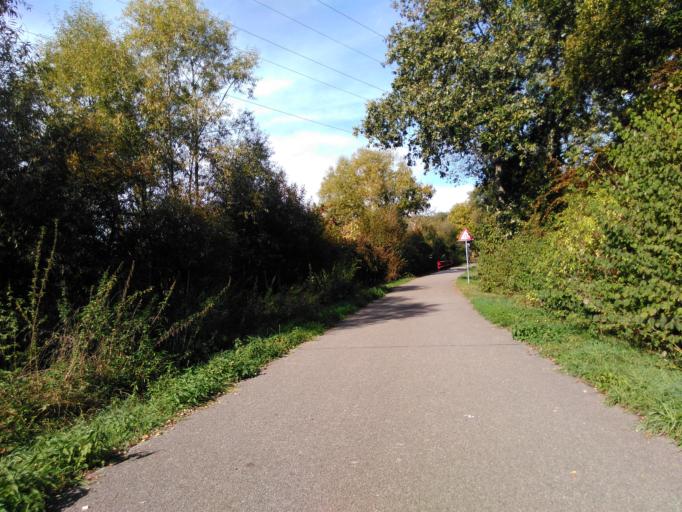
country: LU
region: Luxembourg
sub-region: Canton d'Esch-sur-Alzette
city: Petange
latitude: 49.5718
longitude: 5.8814
